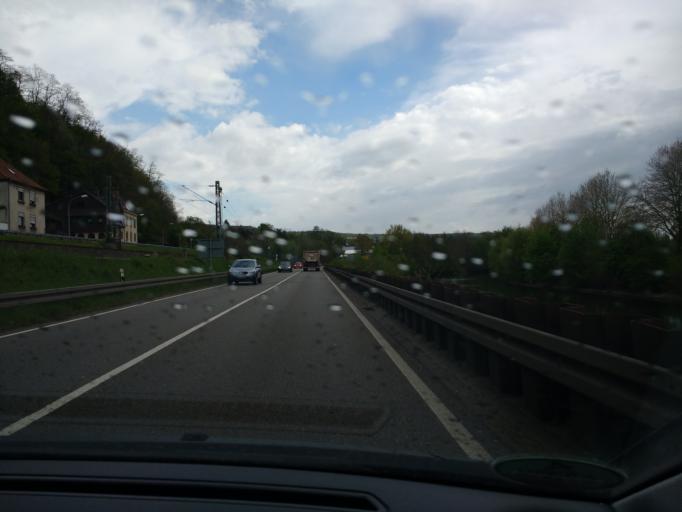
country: DE
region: Saarland
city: Kleinblittersdorf
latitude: 49.1934
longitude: 7.0339
